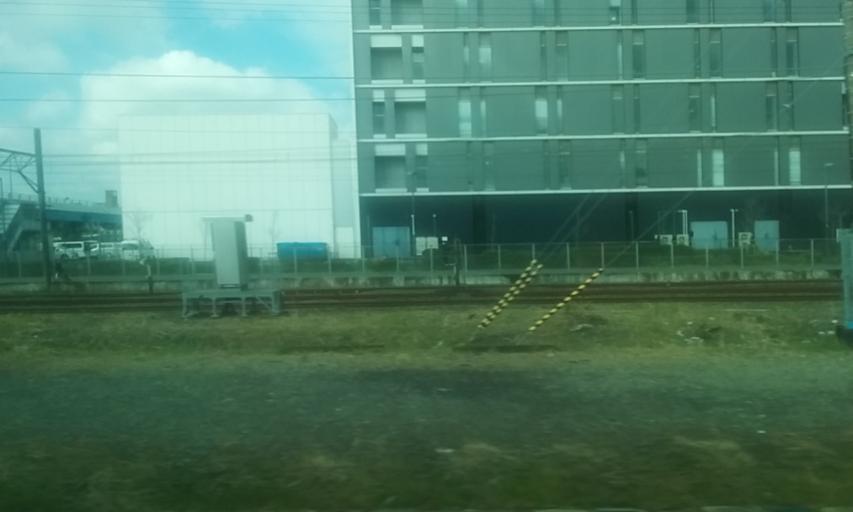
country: JP
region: Kanagawa
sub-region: Kawasaki-shi
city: Kawasaki
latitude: 35.5432
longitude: 139.6747
